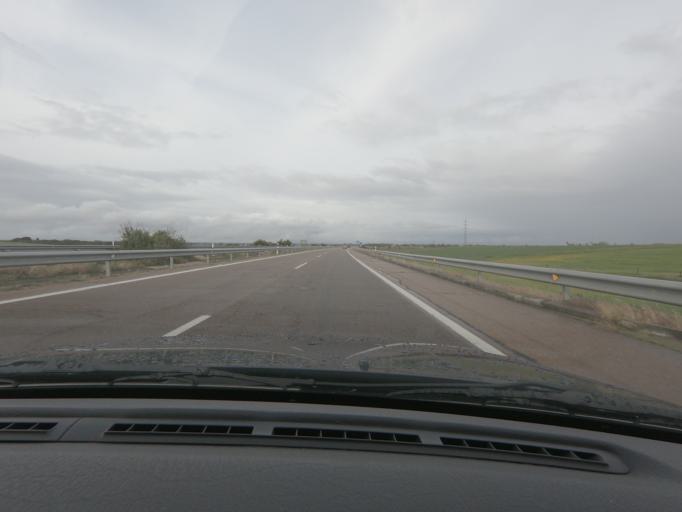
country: ES
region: Extremadura
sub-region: Provincia de Badajoz
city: Badajoz
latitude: 38.9158
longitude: -6.9833
